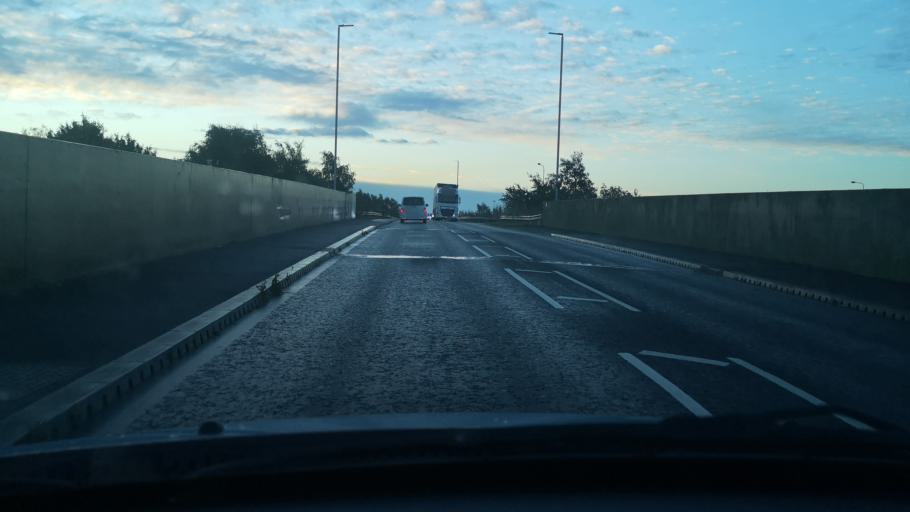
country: GB
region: England
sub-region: East Riding of Yorkshire
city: Airmyn
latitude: 53.7001
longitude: -0.8867
